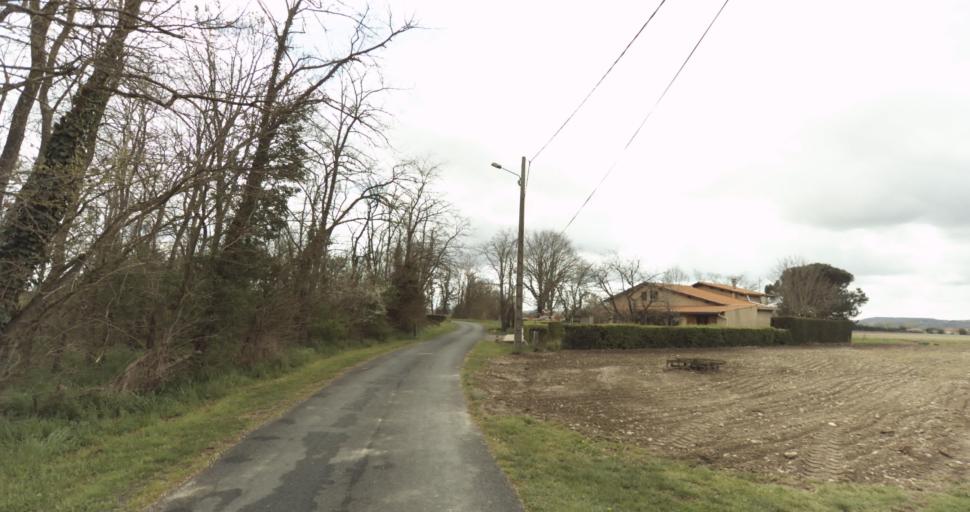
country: FR
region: Midi-Pyrenees
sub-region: Departement de la Haute-Garonne
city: Auterive
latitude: 43.3322
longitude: 1.4839
